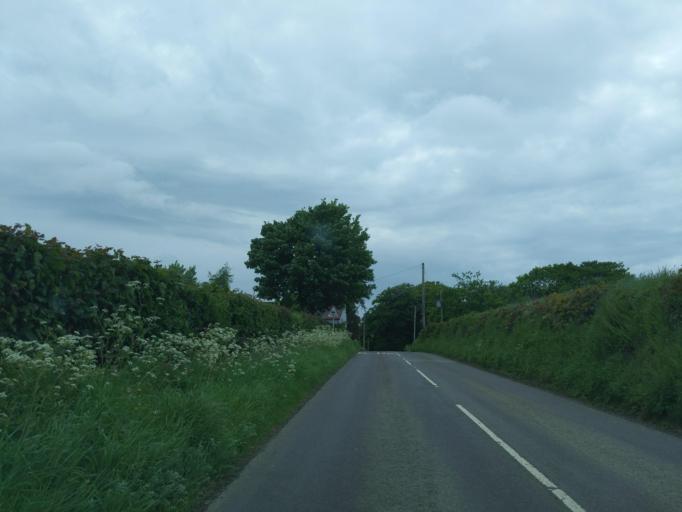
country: GB
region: England
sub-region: Devon
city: Horrabridge
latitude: 50.5182
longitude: -4.1076
